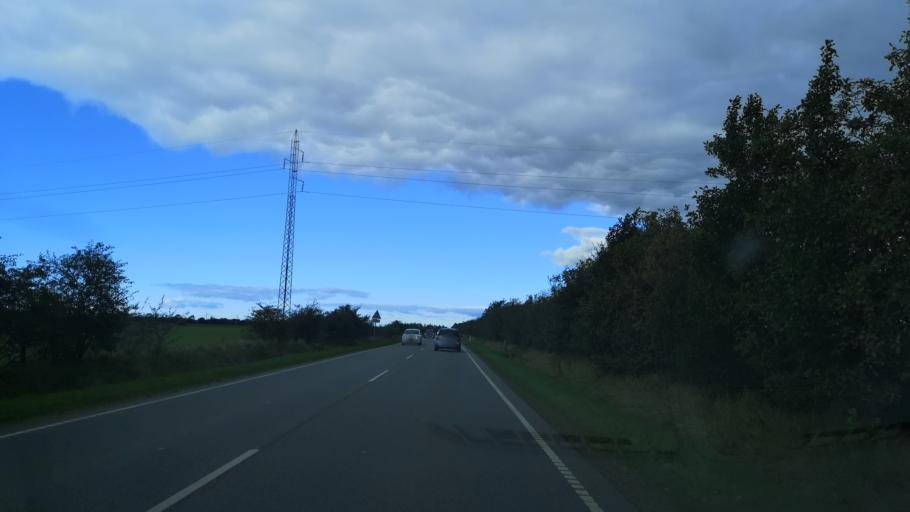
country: DK
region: South Denmark
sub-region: Tonder Kommune
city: Sherrebek
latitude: 55.0642
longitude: 8.8310
